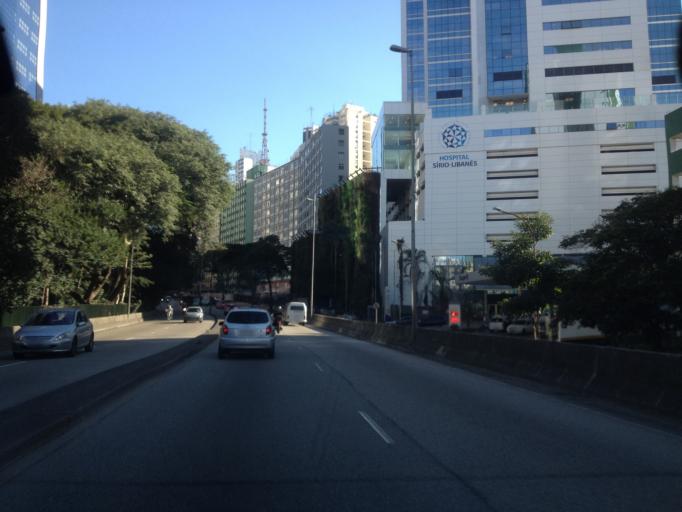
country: BR
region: Sao Paulo
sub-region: Sao Paulo
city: Sao Paulo
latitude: -23.5570
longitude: -46.6519
